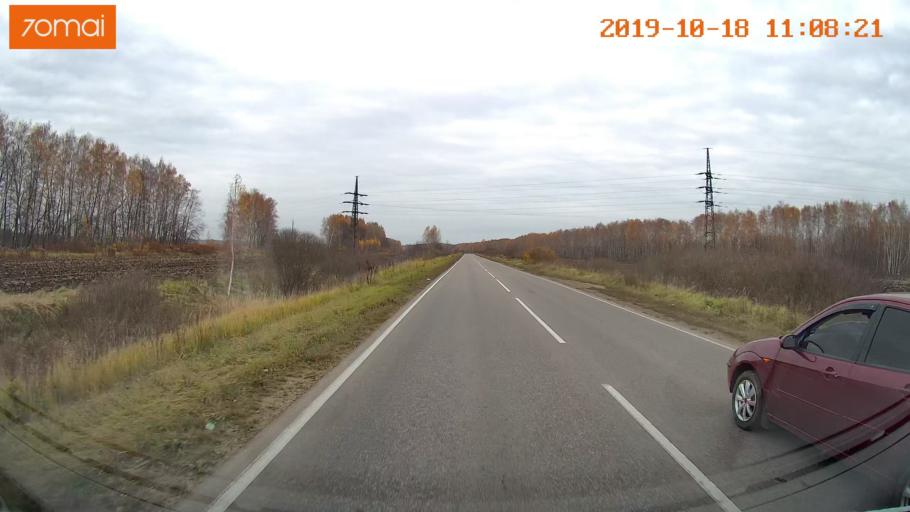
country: RU
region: Tula
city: Kimovsk
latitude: 53.9366
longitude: 38.5377
